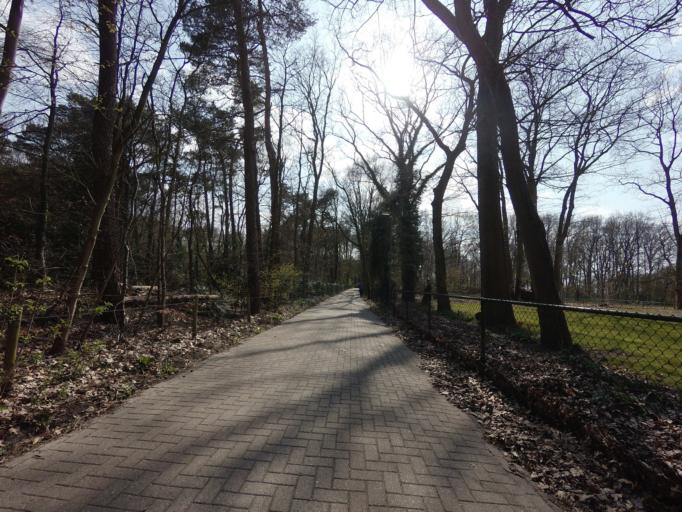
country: NL
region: Gelderland
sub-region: Gemeente Nunspeet
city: Nunspeet
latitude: 52.3616
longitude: 5.7406
